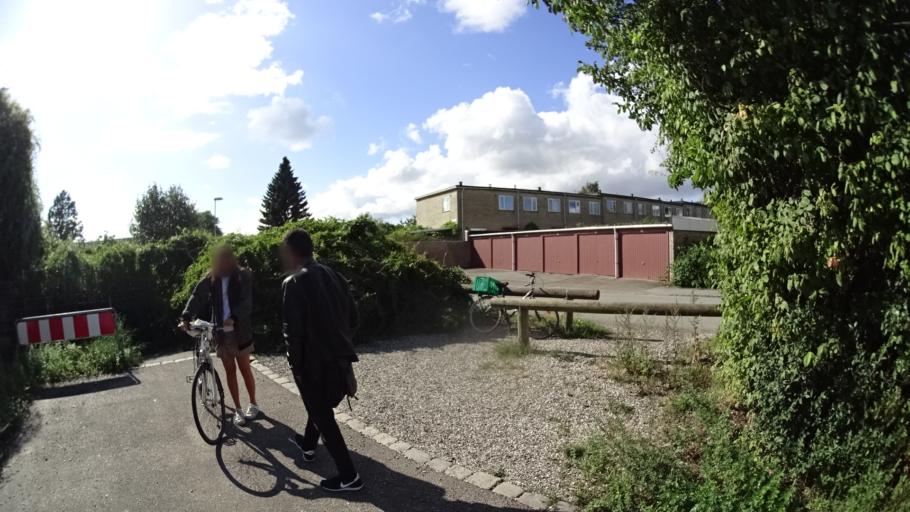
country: DK
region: Central Jutland
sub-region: Arhus Kommune
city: Arhus
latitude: 56.1627
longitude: 10.1725
